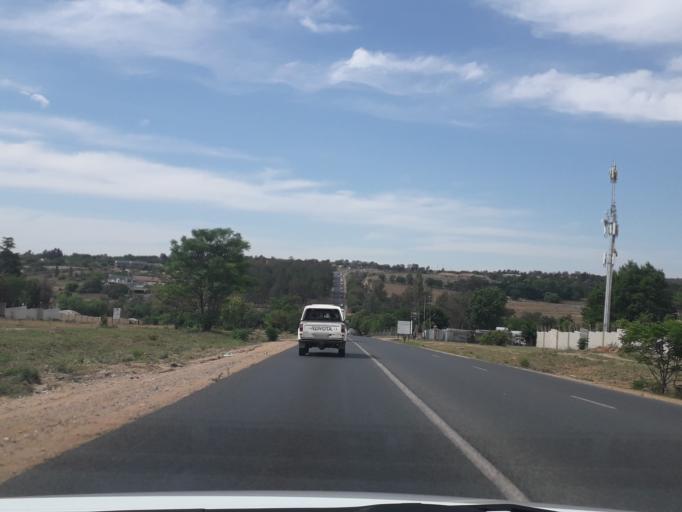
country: ZA
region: Gauteng
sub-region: City of Johannesburg Metropolitan Municipality
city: Diepsloot
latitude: -26.0135
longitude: 28.0359
